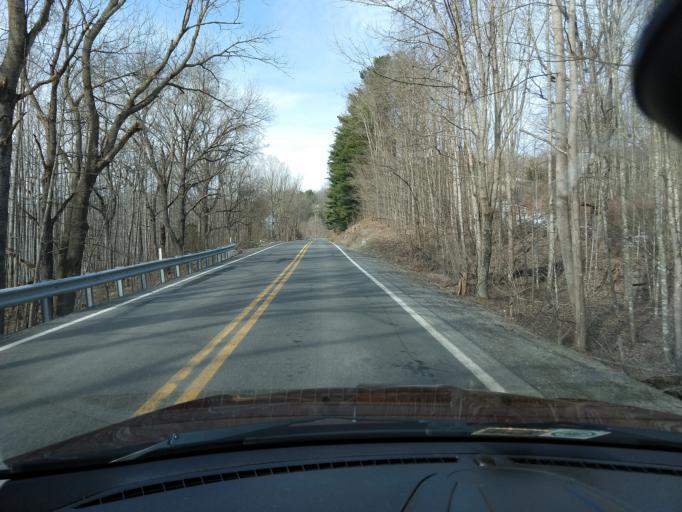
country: US
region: West Virginia
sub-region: Pocahontas County
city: Marlinton
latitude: 38.1173
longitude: -80.2525
